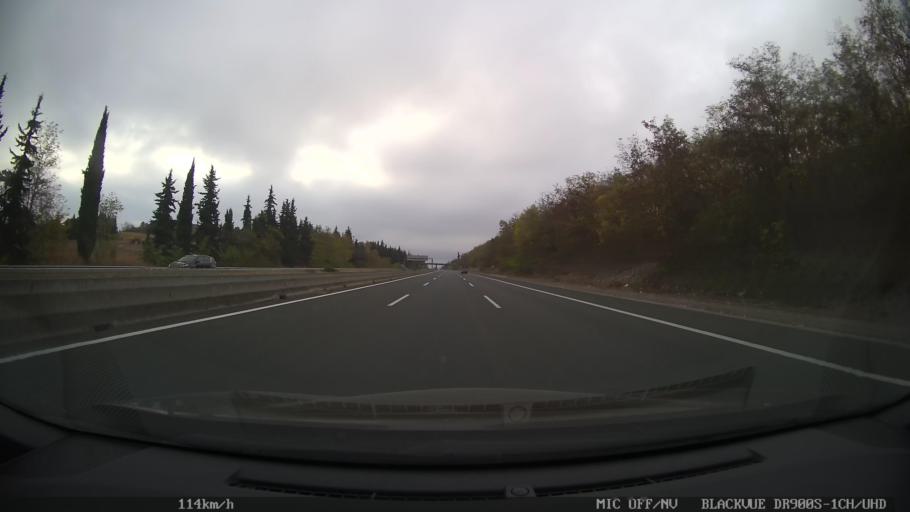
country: GR
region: Central Macedonia
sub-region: Nomos Pierias
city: Makrygialos
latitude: 40.4496
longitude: 22.5808
